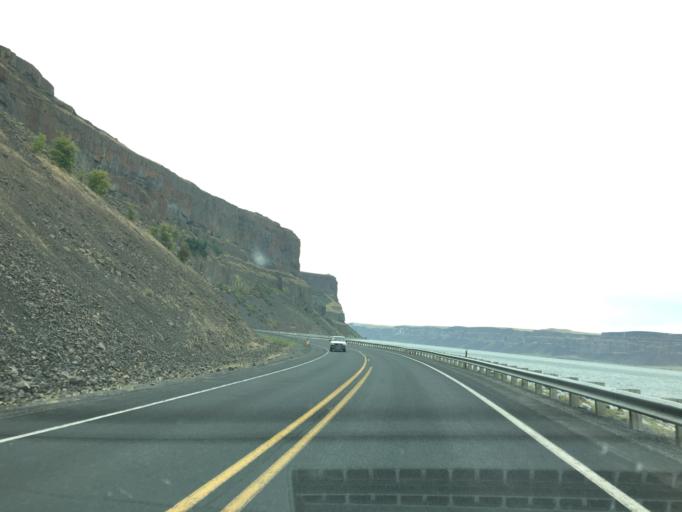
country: US
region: Washington
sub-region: Okanogan County
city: Coulee Dam
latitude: 47.8144
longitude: -119.1593
